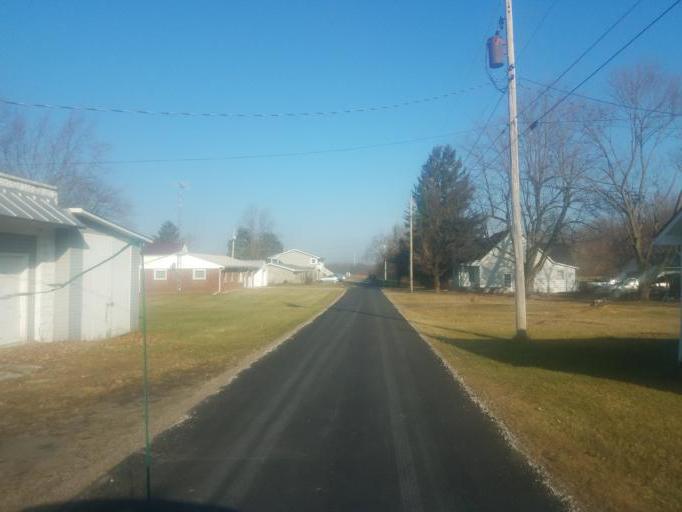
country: US
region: Ohio
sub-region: Seneca County
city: Tiffin
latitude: 41.0539
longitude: -83.0178
